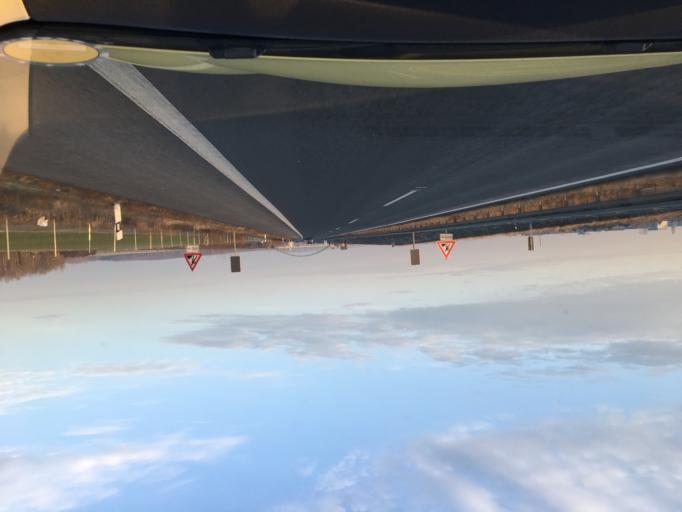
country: DE
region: Saxony
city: Borna
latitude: 51.1167
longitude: 12.5183
